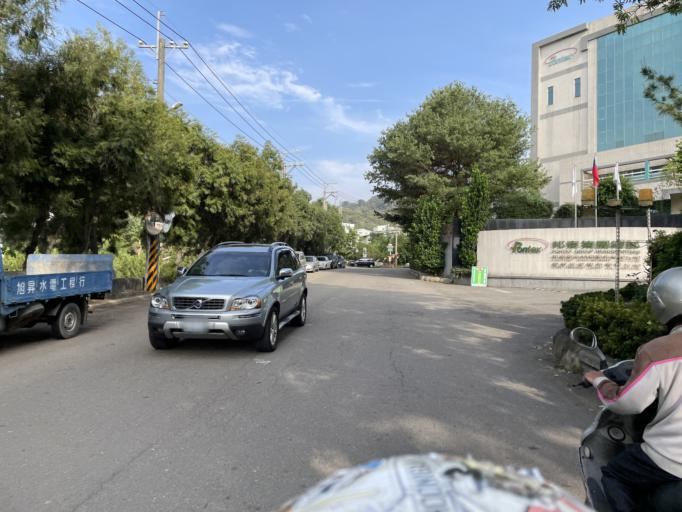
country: TW
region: Taiwan
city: Fengyuan
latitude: 24.2176
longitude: 120.7269
